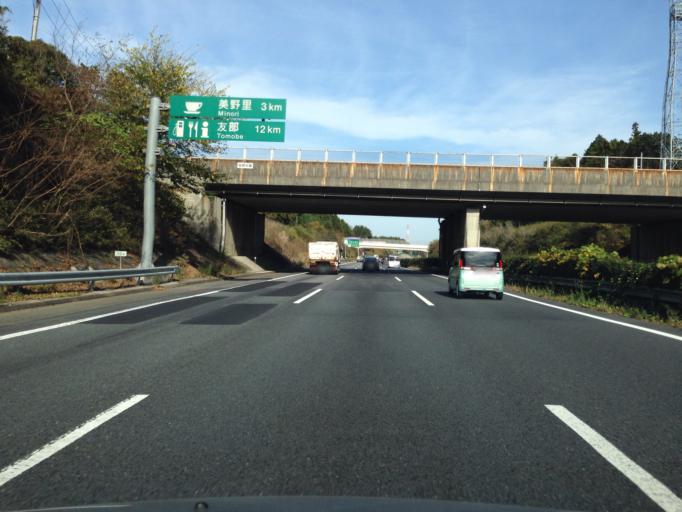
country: JP
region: Ibaraki
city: Ishioka
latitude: 36.2130
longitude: 140.2744
